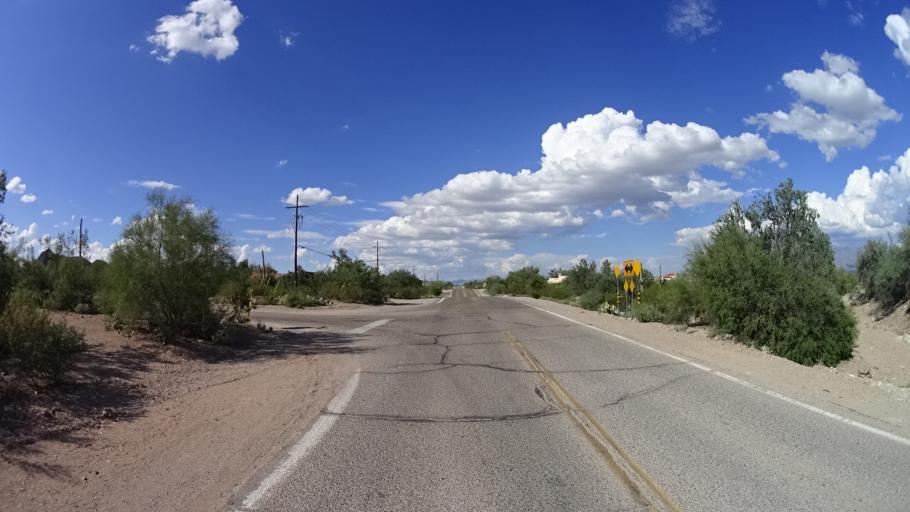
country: US
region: Arizona
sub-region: Pima County
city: Tucson Estates
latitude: 32.2424
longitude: -111.0628
